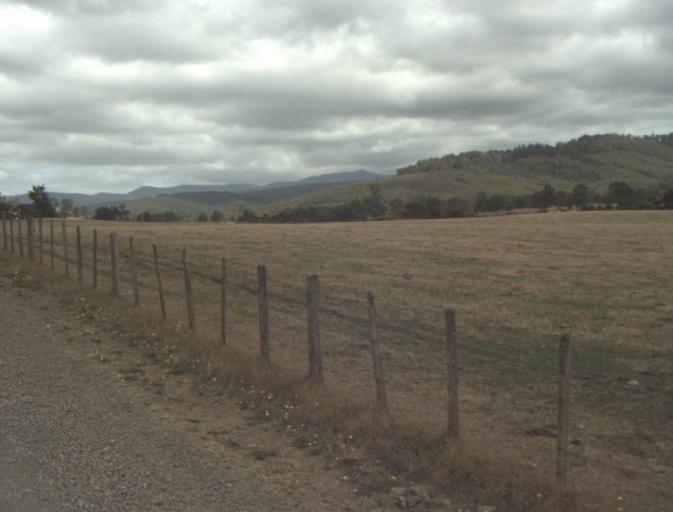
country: AU
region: Tasmania
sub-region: Dorset
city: Scottsdale
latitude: -41.4725
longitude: 147.5870
